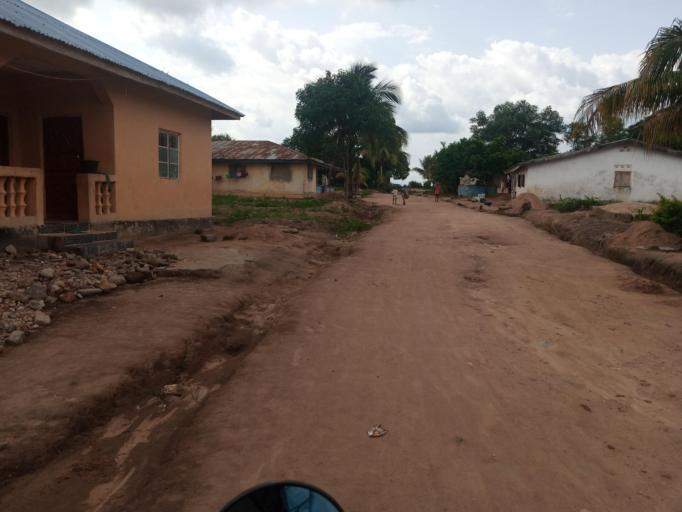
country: SL
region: Southern Province
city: Bo
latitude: 7.9835
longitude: -11.7406
